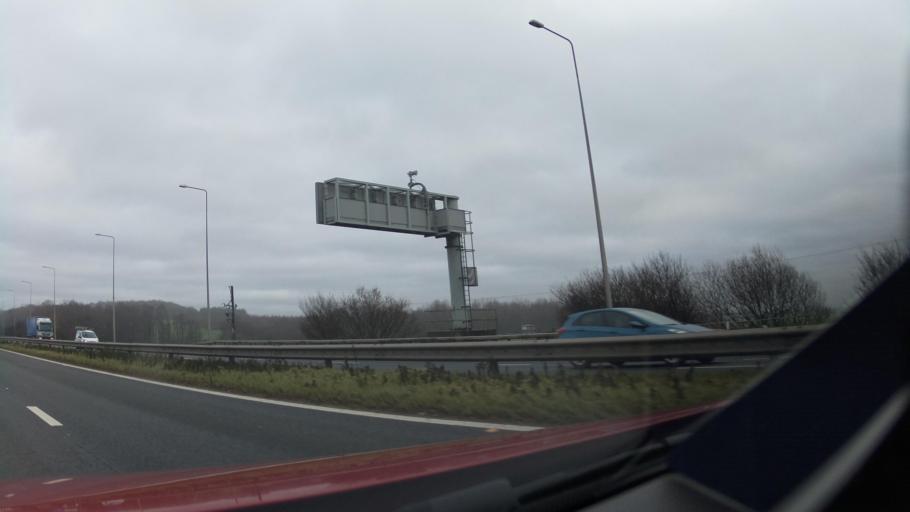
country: GB
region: England
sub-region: Borough of Wigan
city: Shevington
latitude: 53.6021
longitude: -2.6911
